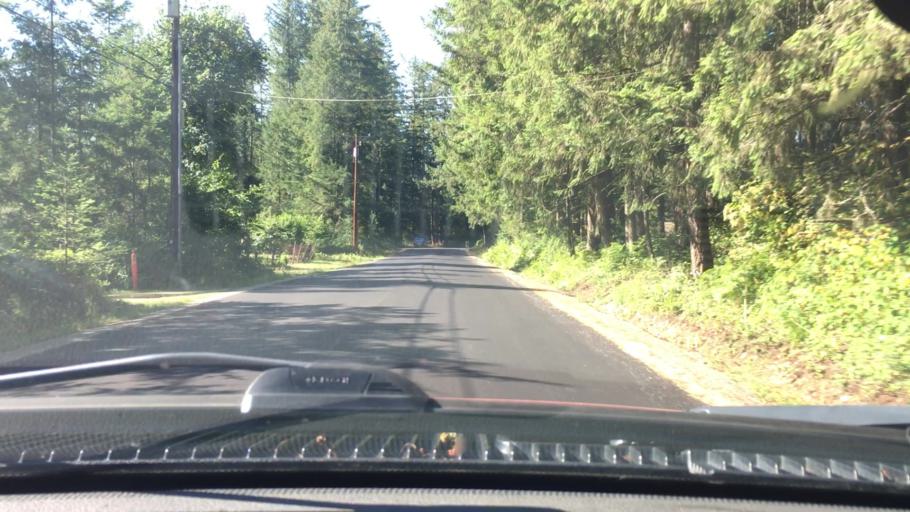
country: US
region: Washington
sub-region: King County
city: Lake Morton-Berrydale
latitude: 47.3191
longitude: -122.0993
